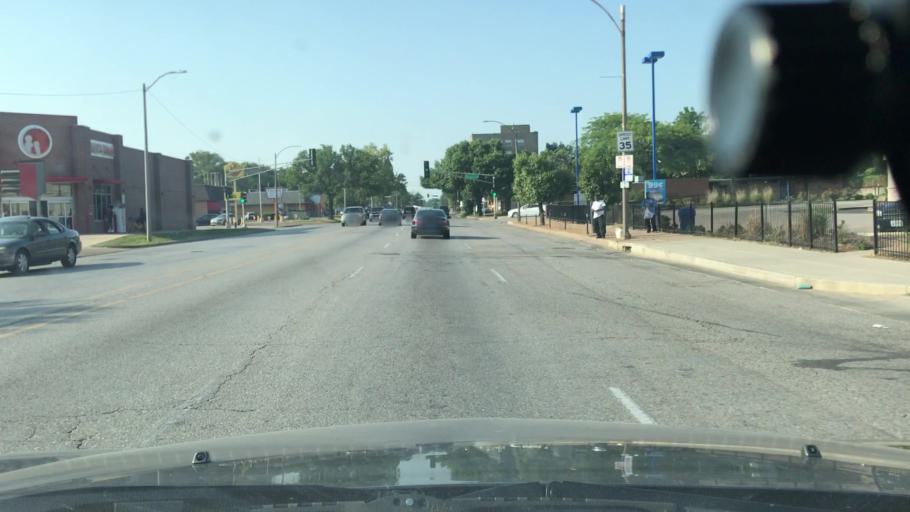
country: US
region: Missouri
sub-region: Saint Louis County
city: Hillsdale
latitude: 38.6520
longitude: -90.2634
